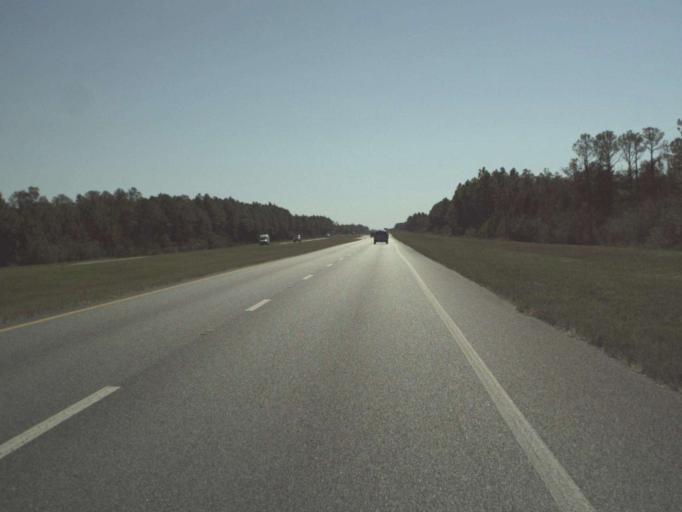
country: US
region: Florida
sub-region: Walton County
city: Seaside
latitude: 30.3054
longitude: -86.0330
